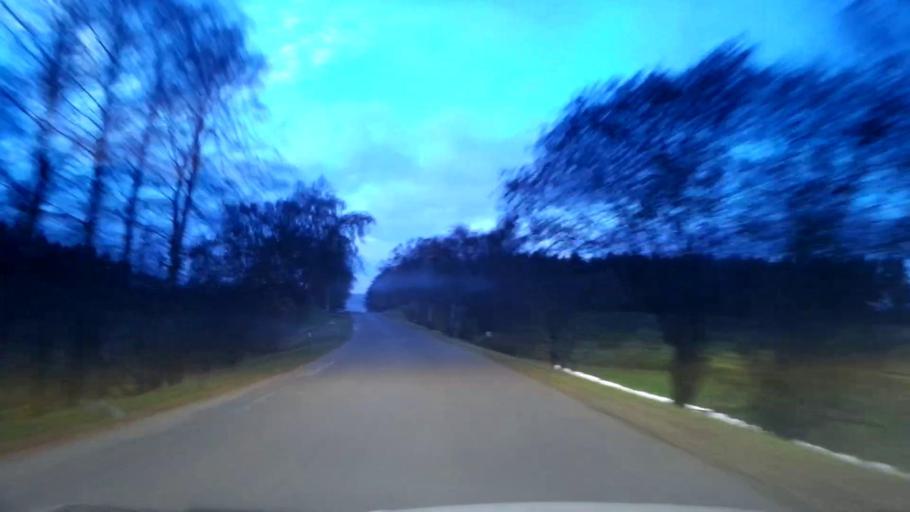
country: DE
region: Bavaria
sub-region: Upper Palatinate
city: Waldershof
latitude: 49.9689
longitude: 12.0827
